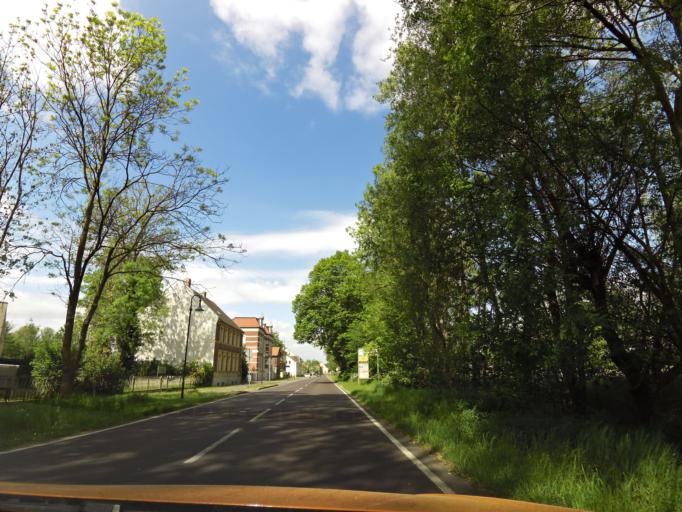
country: DE
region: Saxony-Anhalt
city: Loburg
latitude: 52.1149
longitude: 12.0895
